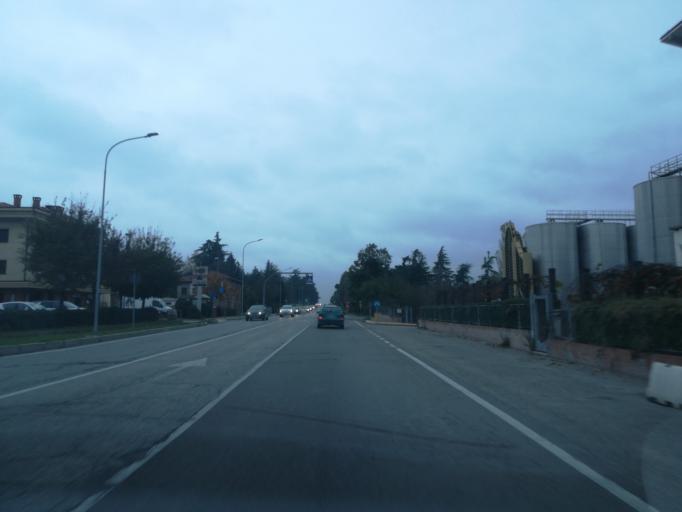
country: IT
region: Emilia-Romagna
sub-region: Provincia di Bologna
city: Toscanella
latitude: 44.3753
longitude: 11.6582
